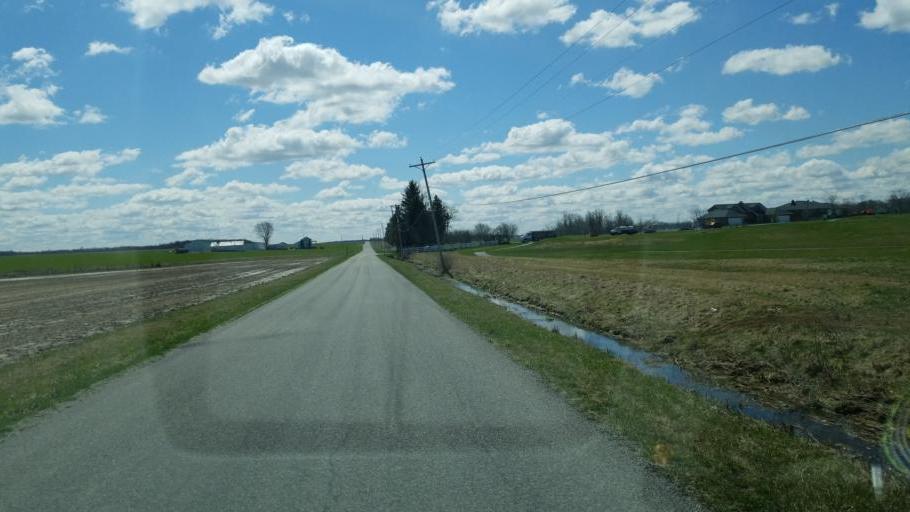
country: US
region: Ohio
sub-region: Seneca County
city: Fostoria
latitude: 41.0648
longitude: -83.5148
